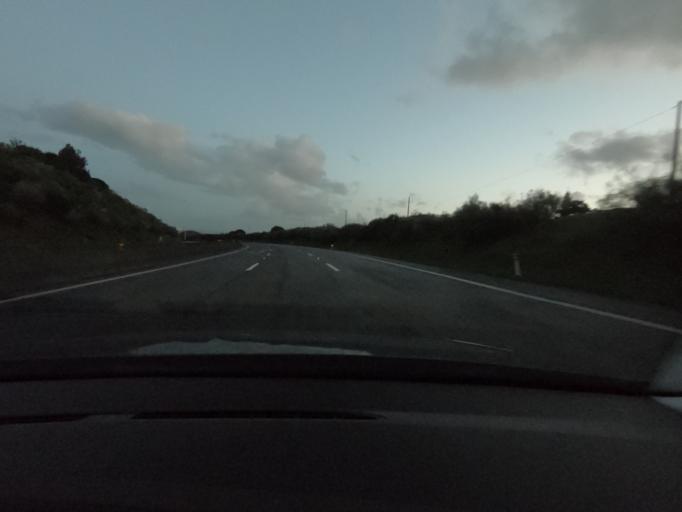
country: PT
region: Lisbon
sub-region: Oeiras
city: Barcarena
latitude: 38.7379
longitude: -9.2780
